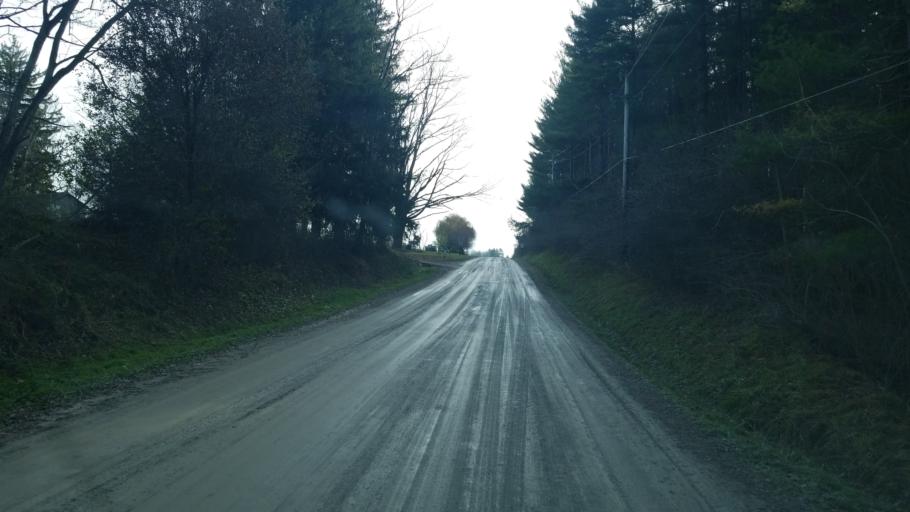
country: US
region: Ohio
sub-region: Ashtabula County
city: Roaming Shores
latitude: 41.6493
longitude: -80.8158
